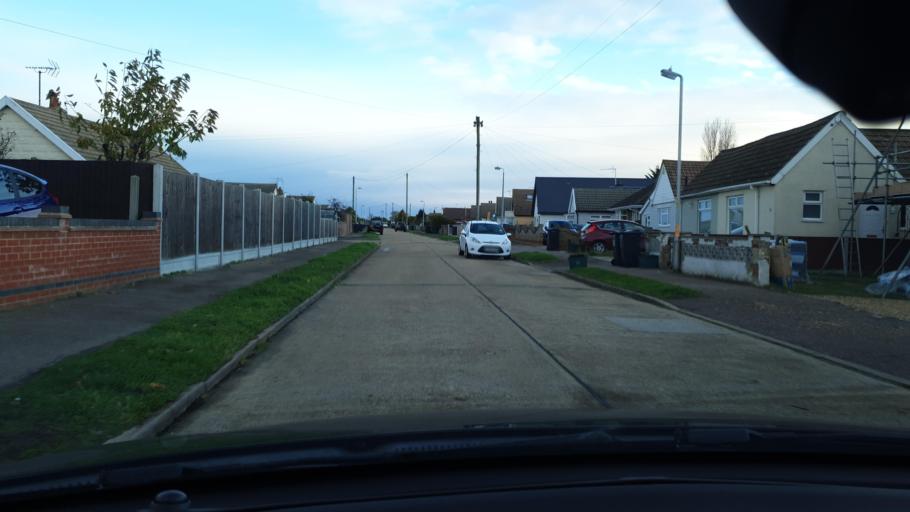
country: GB
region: England
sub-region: Essex
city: Clacton-on-Sea
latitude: 51.8089
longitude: 1.1707
